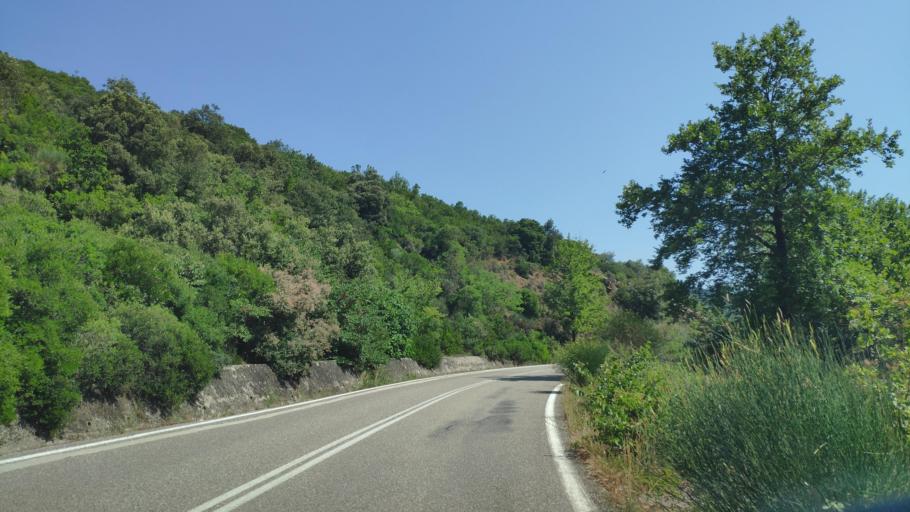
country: GR
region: West Greece
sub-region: Nomos Aitolias kai Akarnanias
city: Lepenou
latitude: 38.7719
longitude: 21.3350
